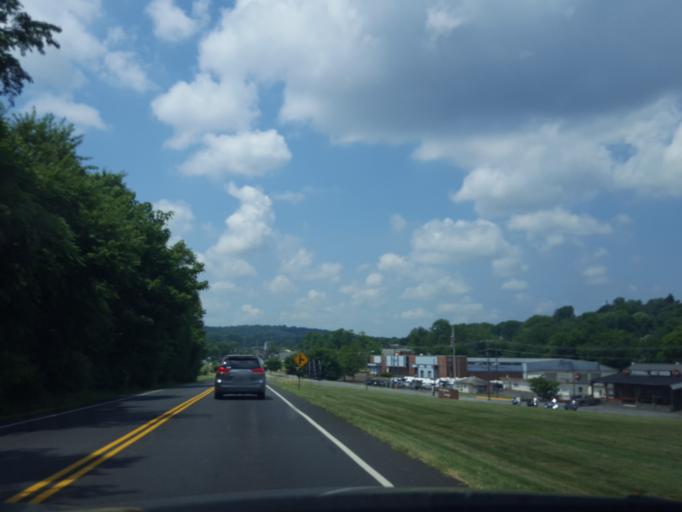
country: US
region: Virginia
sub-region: Orange County
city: Orange
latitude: 38.2429
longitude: -78.0954
